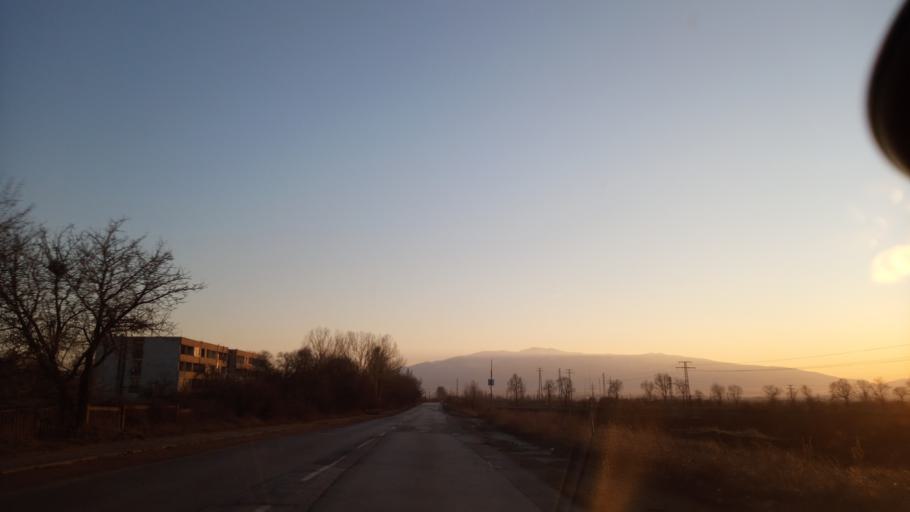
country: BG
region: Sofia-Capital
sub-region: Stolichna Obshtina
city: Bukhovo
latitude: 42.7574
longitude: 23.4855
